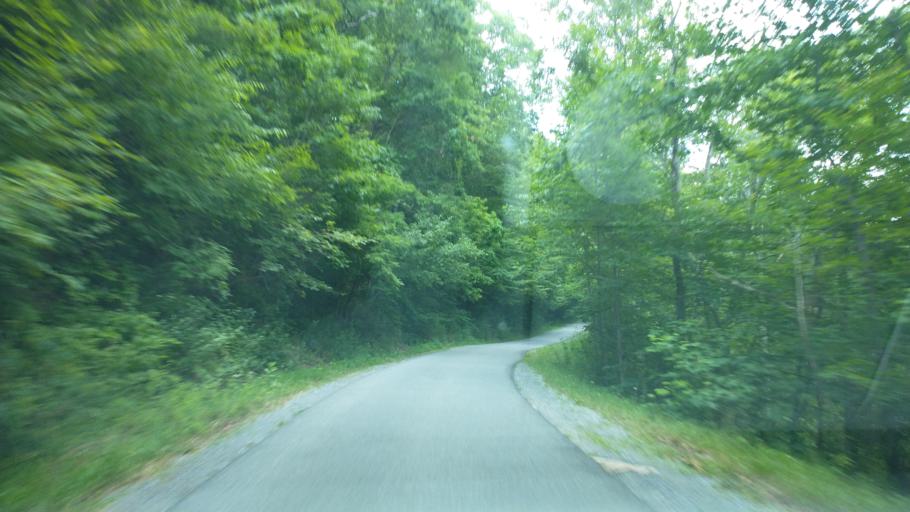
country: US
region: West Virginia
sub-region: Mercer County
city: Athens
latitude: 37.4622
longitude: -81.0616
